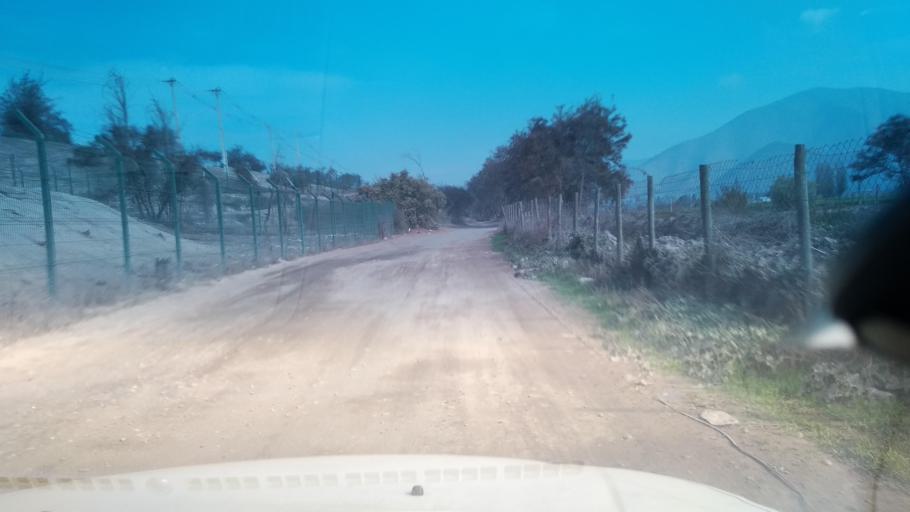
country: CL
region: Santiago Metropolitan
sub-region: Provincia de Santiago
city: Lo Prado
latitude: -33.4637
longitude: -70.7848
